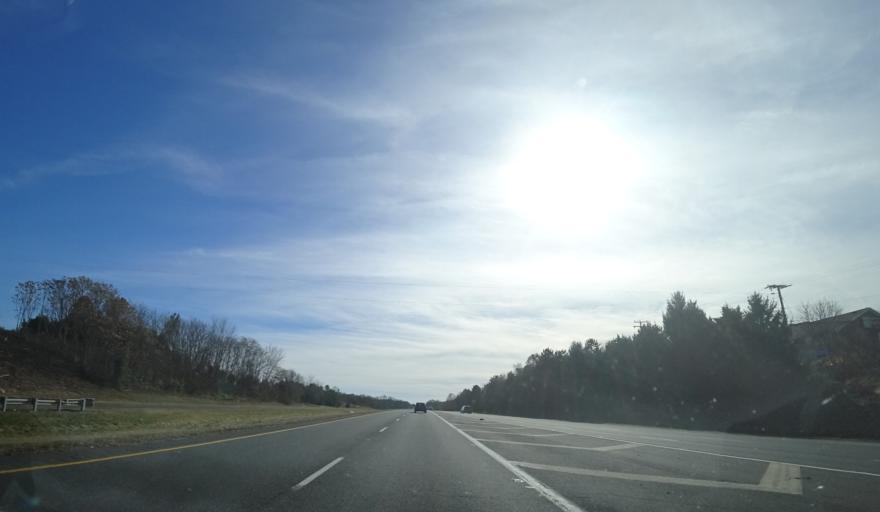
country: US
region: Virginia
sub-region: Fauquier County
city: Warrenton
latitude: 38.7233
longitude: -77.7815
